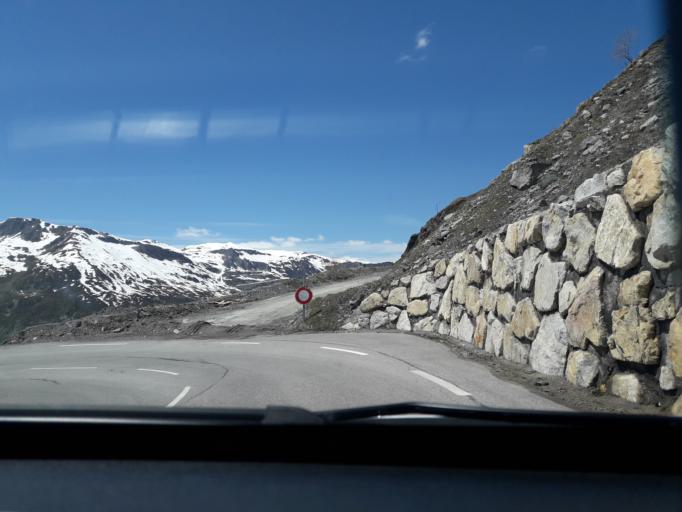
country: FR
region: Rhone-Alpes
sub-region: Departement de la Savoie
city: Val Thorens
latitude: 45.3009
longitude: 6.5649
